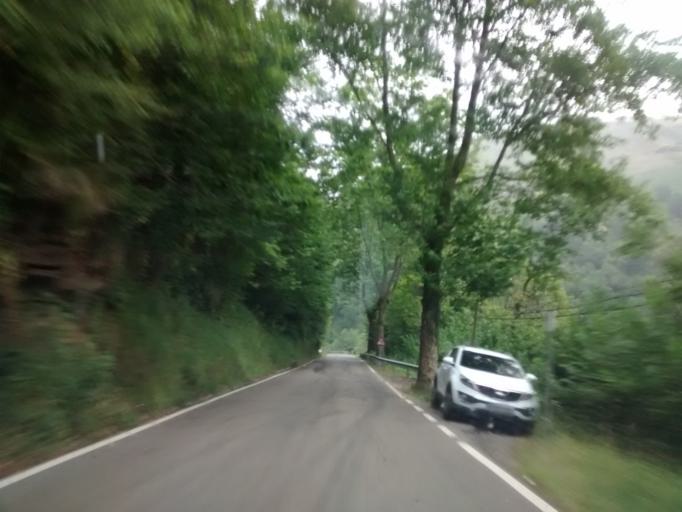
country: ES
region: Cantabria
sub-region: Provincia de Cantabria
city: San Pedro del Romeral
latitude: 43.1688
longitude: -3.8618
